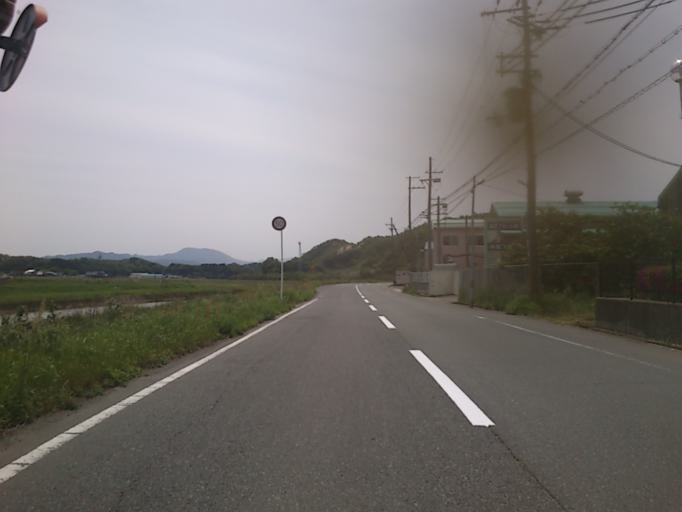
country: JP
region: Kyoto
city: Miyazu
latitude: 35.6512
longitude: 135.0889
